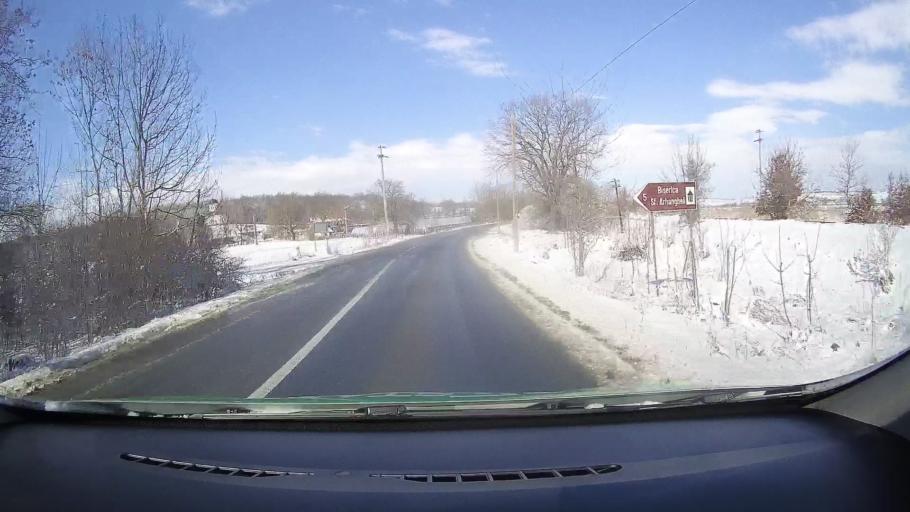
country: RO
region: Sibiu
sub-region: Comuna Nocrich
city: Nocrich
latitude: 45.8704
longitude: 24.4515
